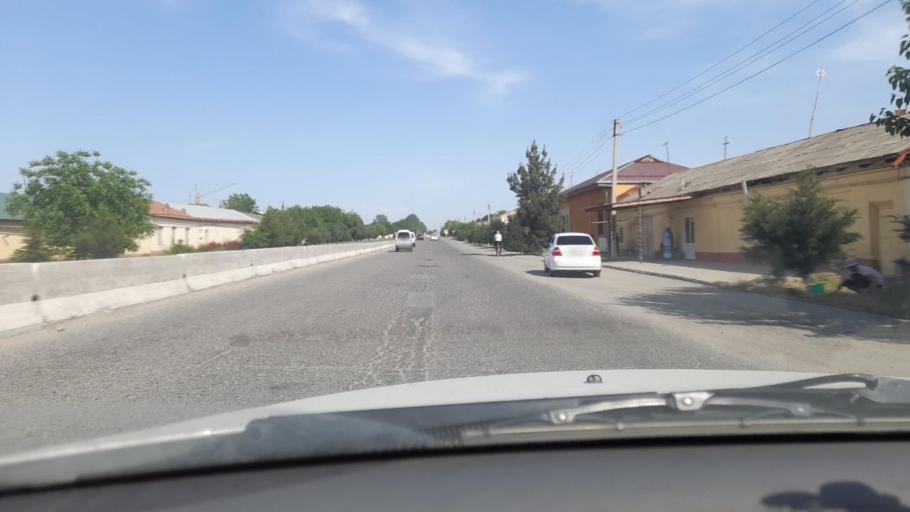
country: UZ
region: Samarqand
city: Daxbet
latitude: 39.7639
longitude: 66.9070
